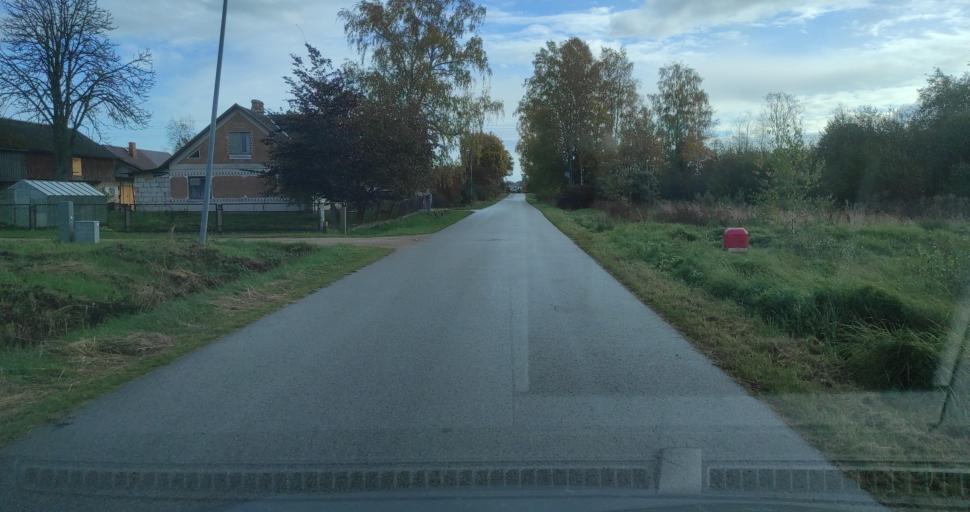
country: LV
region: Skrunda
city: Skrunda
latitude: 56.6720
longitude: 22.0073
